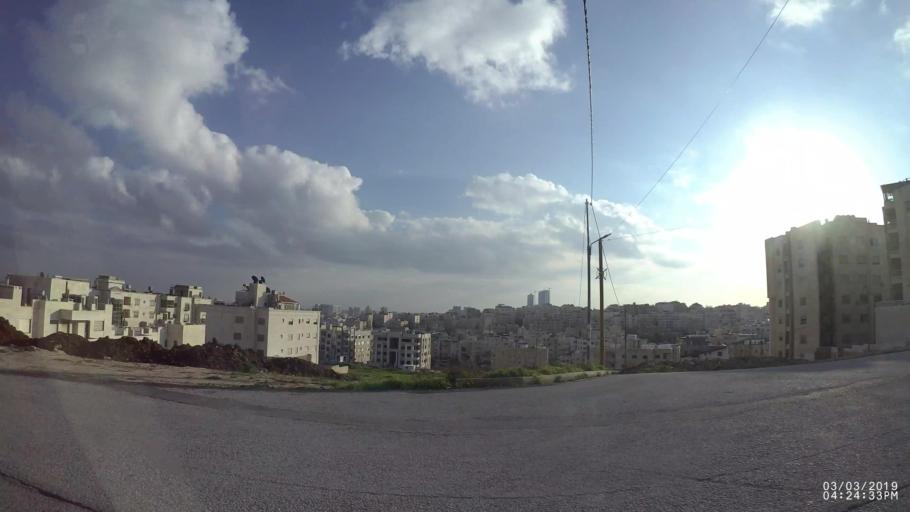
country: JO
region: Amman
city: Al Jubayhah
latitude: 31.9808
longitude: 35.8849
